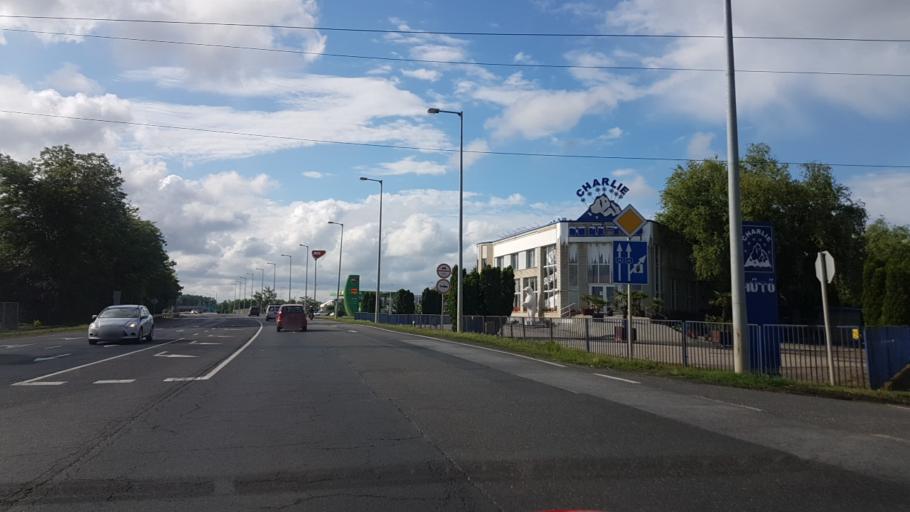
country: HU
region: Hajdu-Bihar
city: Debrecen
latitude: 47.5676
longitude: 21.5982
